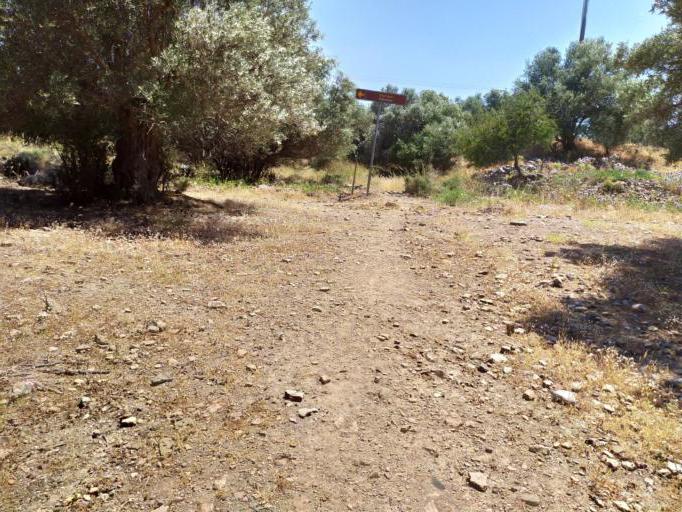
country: GR
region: Crete
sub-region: Nomos Irakleiou
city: Agioi Deka
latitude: 35.0599
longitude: 24.9503
